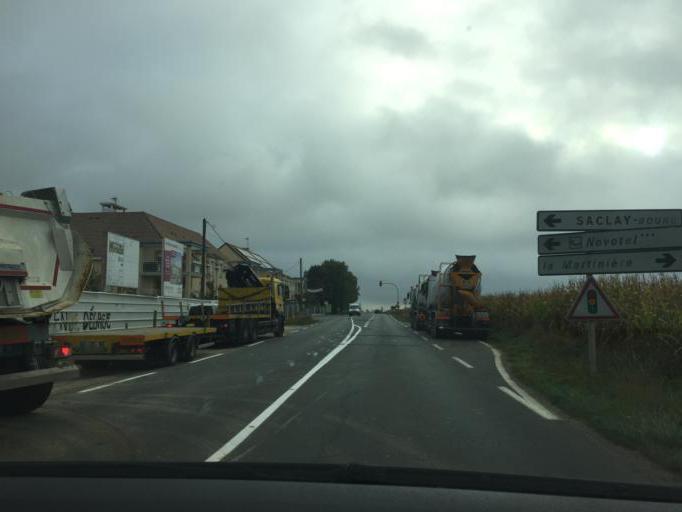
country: FR
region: Ile-de-France
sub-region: Departement de l'Essonne
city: Saclay
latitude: 48.7287
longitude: 2.1735
